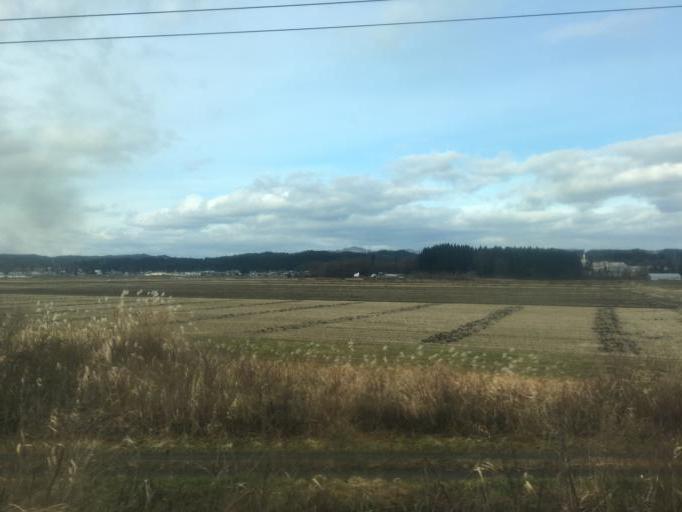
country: JP
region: Akita
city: Takanosu
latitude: 40.2476
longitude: 140.3939
